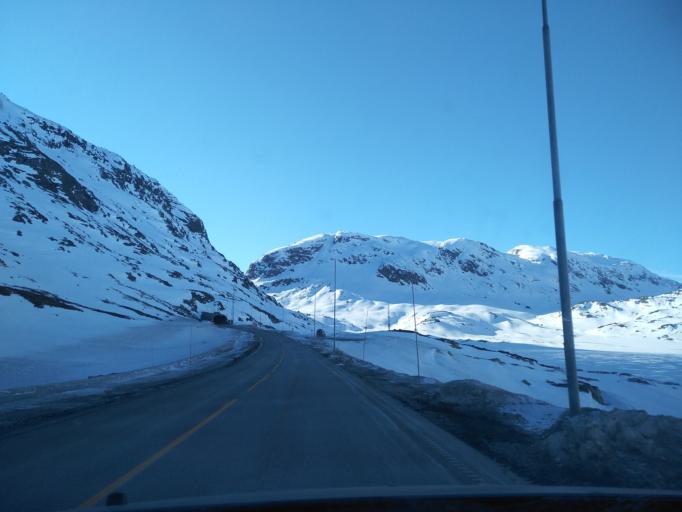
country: NO
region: Aust-Agder
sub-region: Bykle
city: Hovden
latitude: 59.8501
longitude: 7.0906
